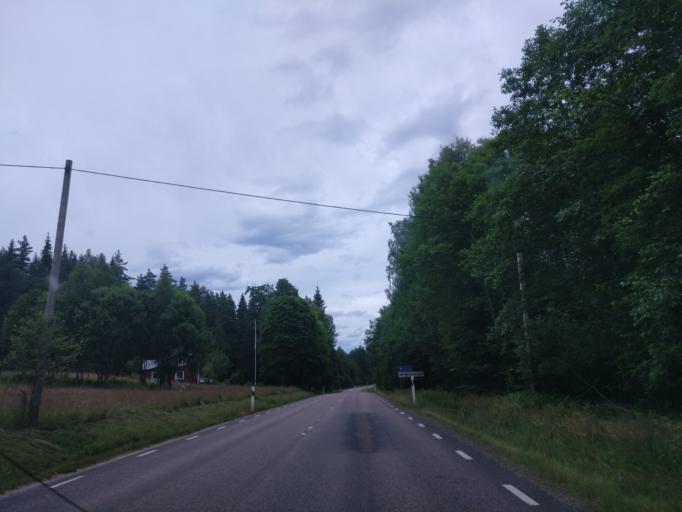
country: SE
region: Vaermland
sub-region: Hagfors Kommun
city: Ekshaerad
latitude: 60.1658
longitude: 13.4774
